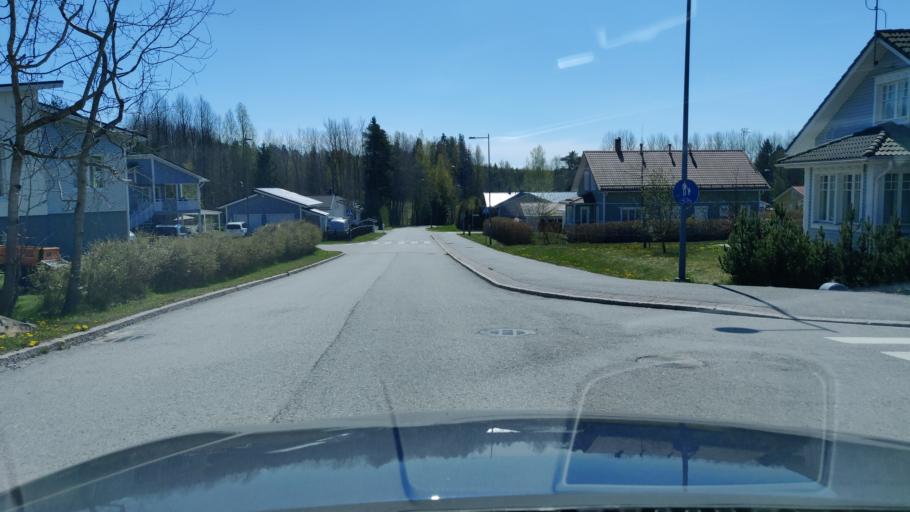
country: FI
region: Uusimaa
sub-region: Helsinki
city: Nurmijaervi
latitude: 60.3624
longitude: 24.7551
